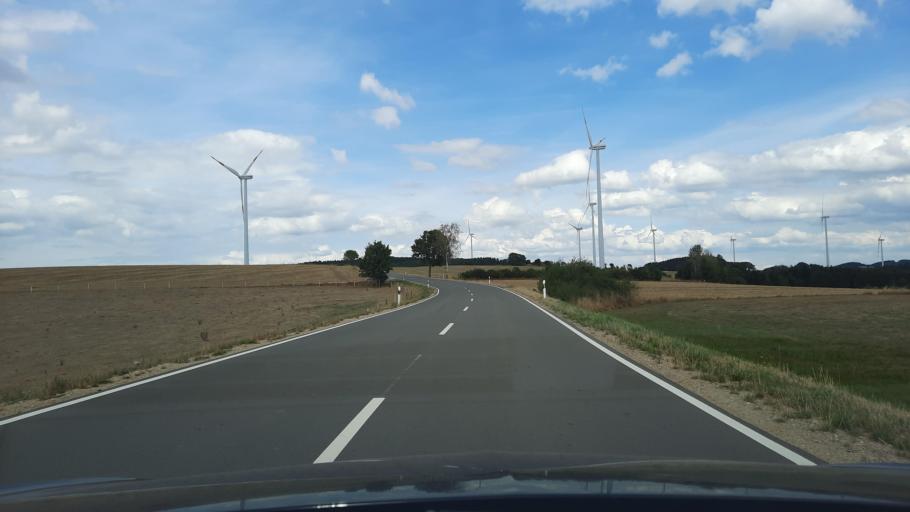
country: DE
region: Rheinland-Pfalz
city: Pronsfeld
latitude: 50.1819
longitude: 6.3262
